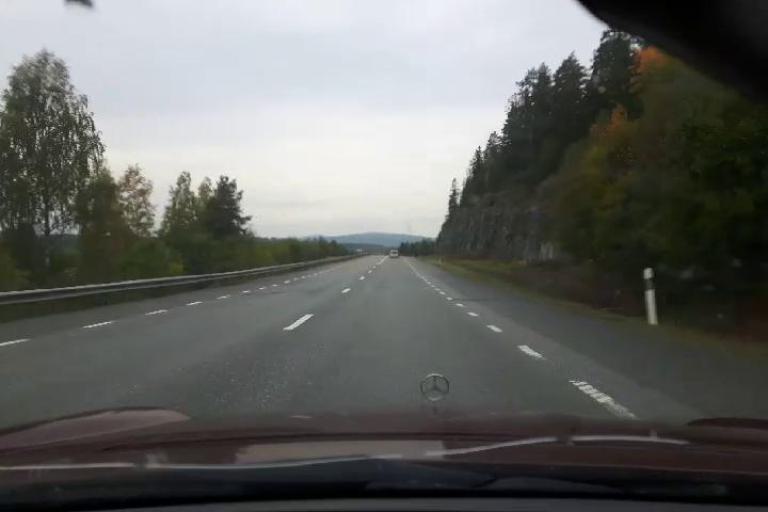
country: SE
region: Vaesternorrland
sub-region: Kramfors Kommun
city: Nordingra
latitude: 63.0066
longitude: 18.2293
